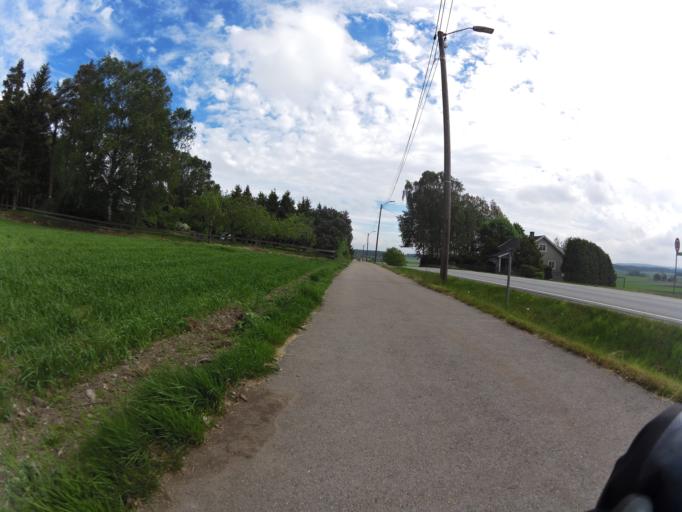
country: NO
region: Ostfold
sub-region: Rade
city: Karlshus
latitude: 59.3644
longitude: 10.8131
